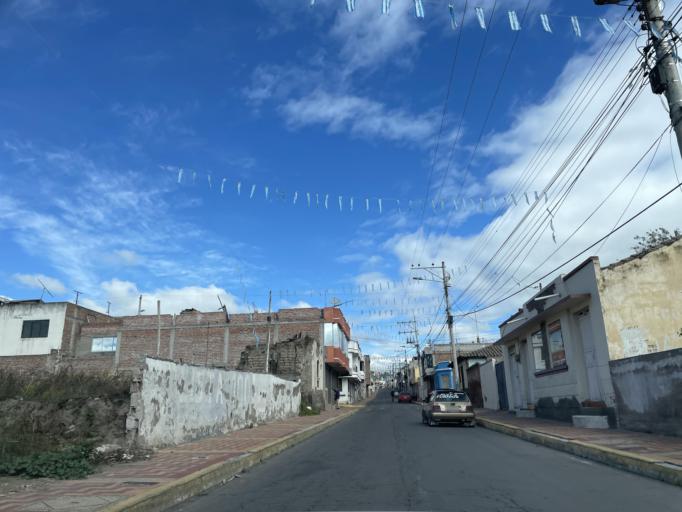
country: EC
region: Chimborazo
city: Guano
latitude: -1.6078
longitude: -78.6352
